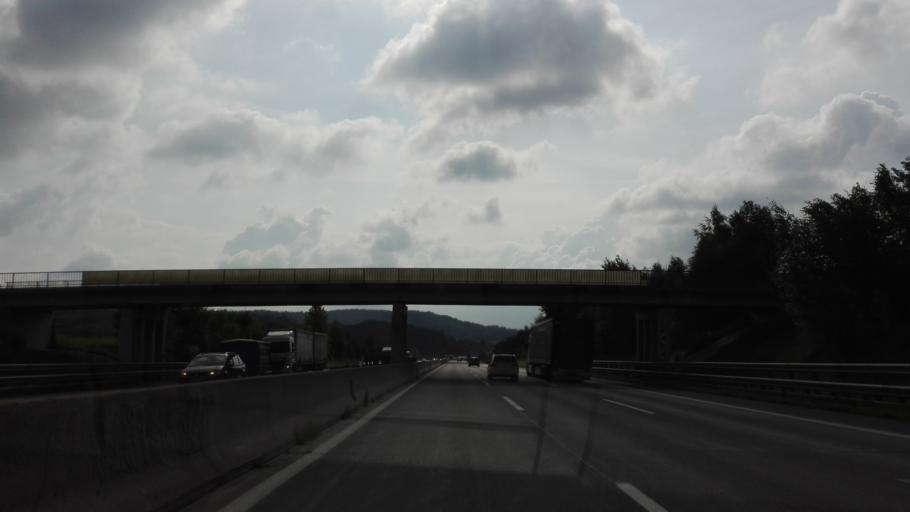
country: AT
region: Lower Austria
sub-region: Politischer Bezirk Melk
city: Blindenmarkt
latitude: 48.1373
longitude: 14.9693
